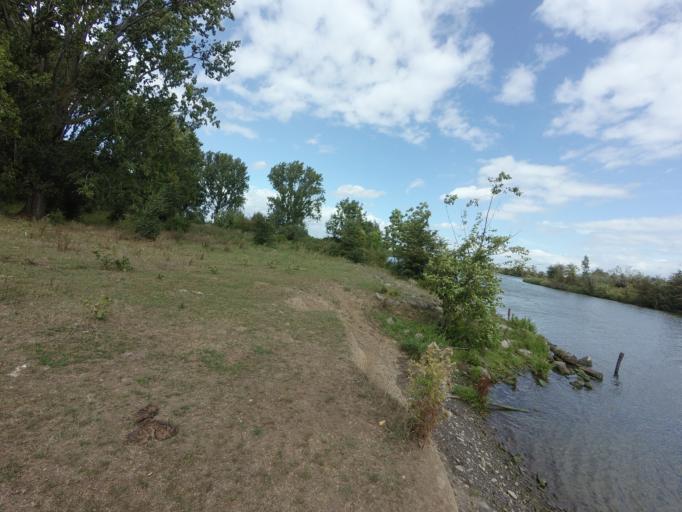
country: NL
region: Limburg
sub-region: Gemeente Maasgouw
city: Maasbracht
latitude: 51.1465
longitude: 5.8722
